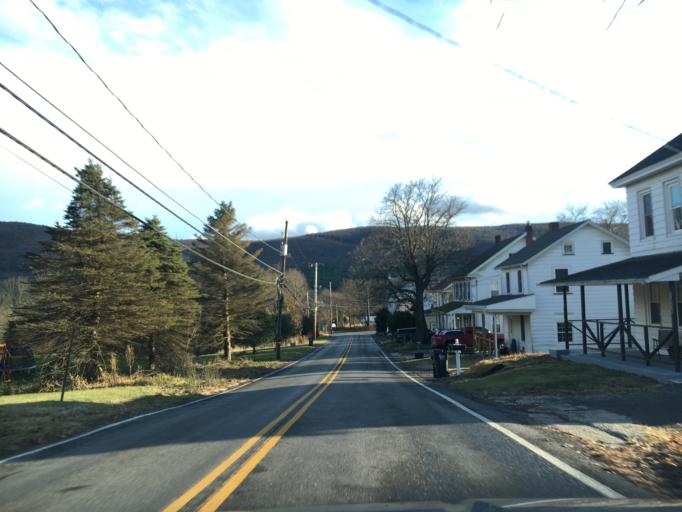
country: US
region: Pennsylvania
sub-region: Carbon County
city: Lehighton
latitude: 40.7857
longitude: -75.7142
